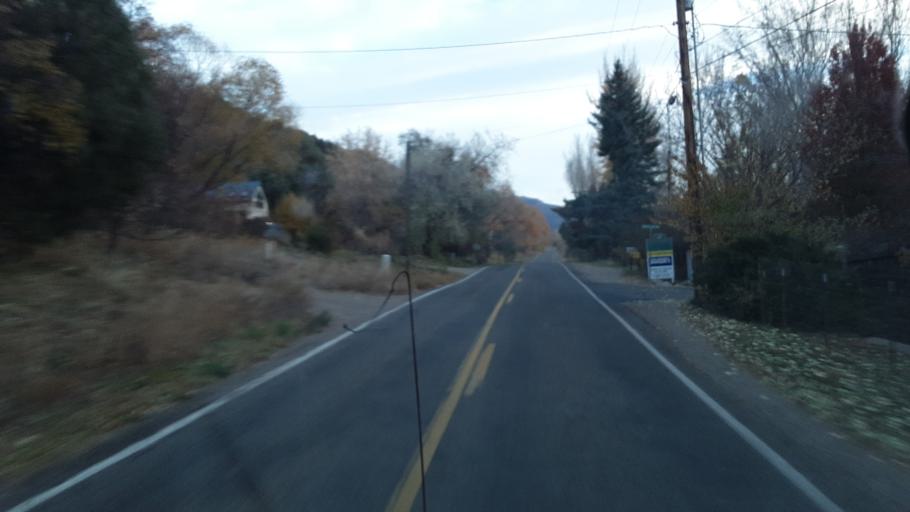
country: US
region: Colorado
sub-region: La Plata County
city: Durango
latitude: 37.3494
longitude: -107.8576
